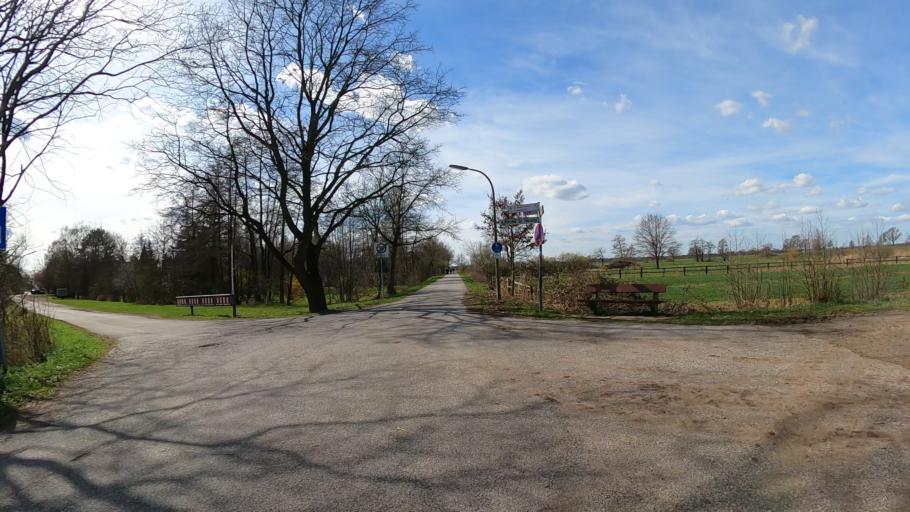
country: DE
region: Lower Saxony
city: Drage
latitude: 53.4312
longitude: 10.2715
